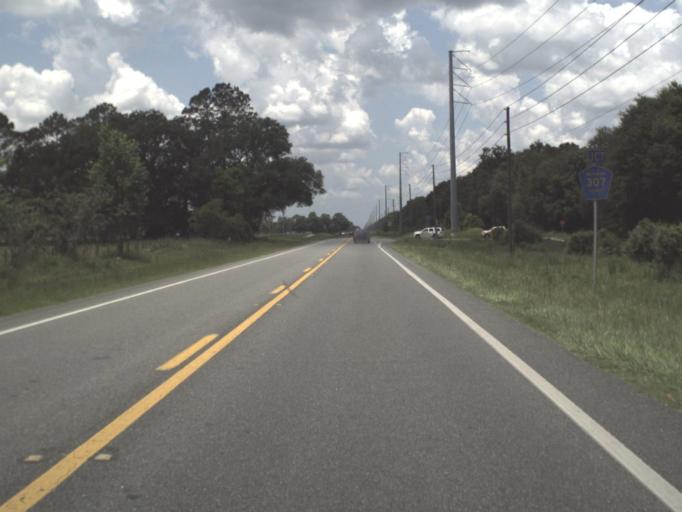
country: US
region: Florida
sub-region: Gilchrist County
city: Trenton
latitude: 29.6131
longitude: -82.8552
